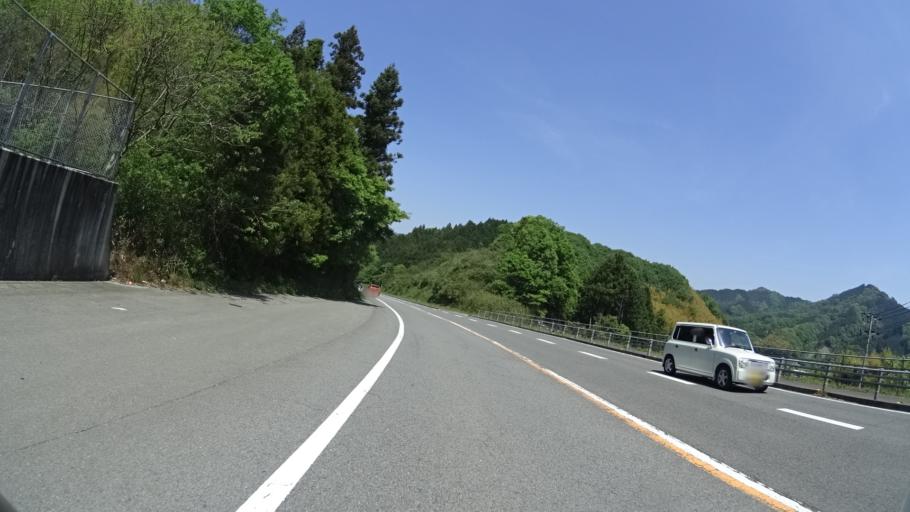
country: JP
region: Ehime
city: Hojo
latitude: 33.9966
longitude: 132.9330
